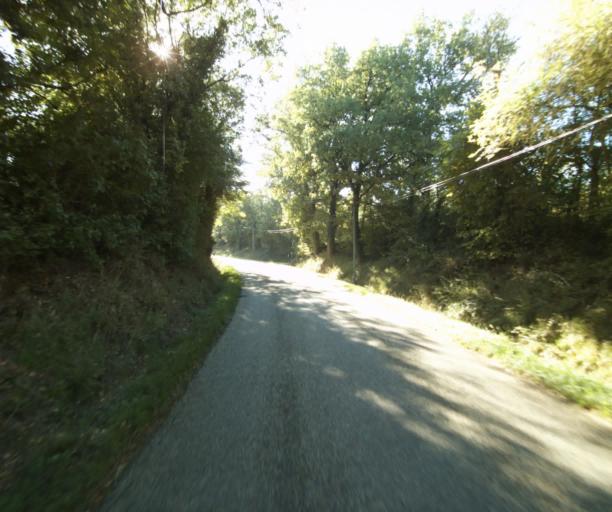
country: FR
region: Midi-Pyrenees
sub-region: Departement du Gers
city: Gondrin
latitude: 43.8320
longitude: 0.2558
